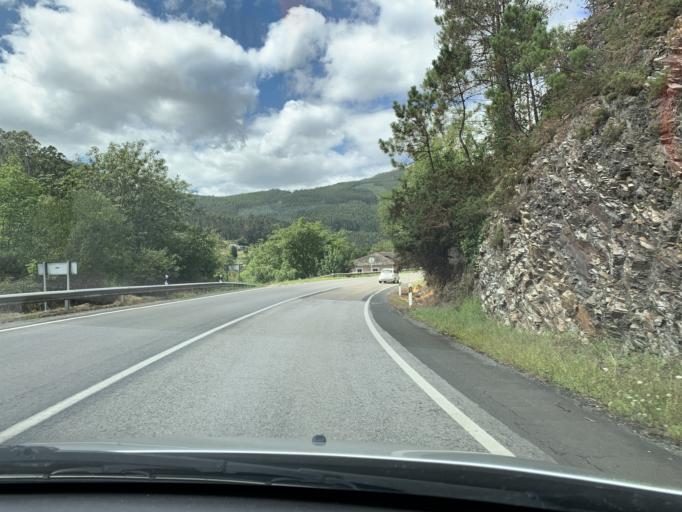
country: ES
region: Galicia
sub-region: Provincia de Lugo
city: Barreiros
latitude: 43.5089
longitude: -7.2743
